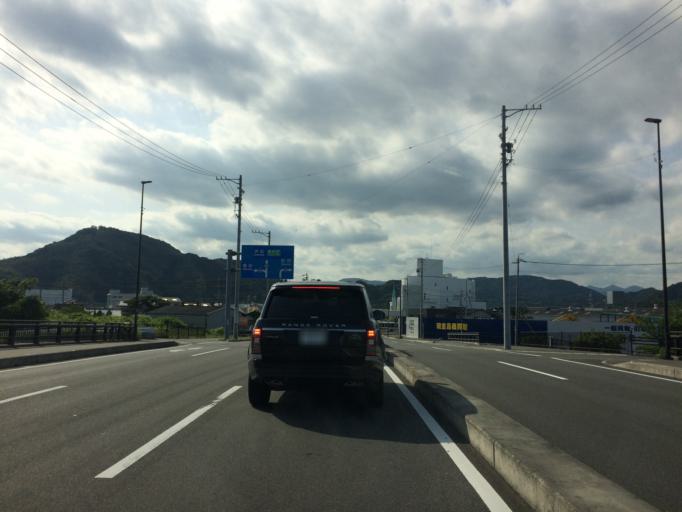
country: JP
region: Shizuoka
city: Fujieda
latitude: 34.8927
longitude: 138.2838
